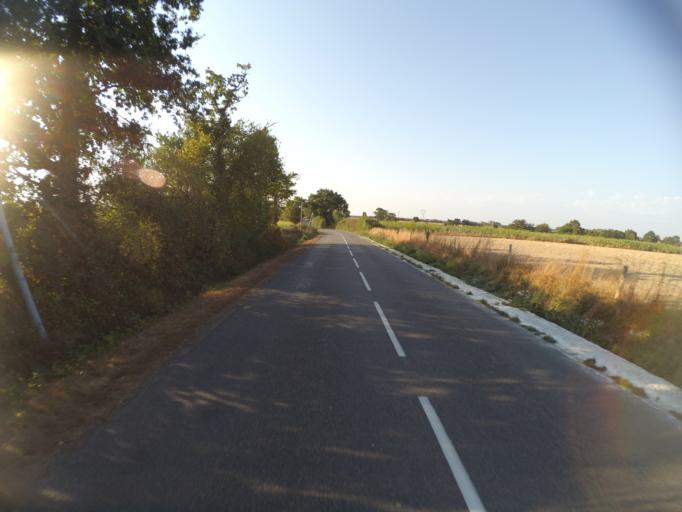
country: FR
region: Pays de la Loire
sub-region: Departement de la Loire-Atlantique
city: La Planche
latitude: 47.0276
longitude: -1.4216
